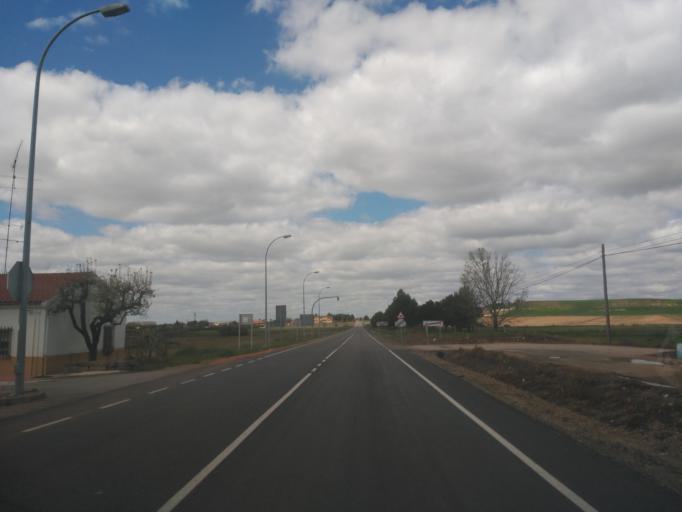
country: ES
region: Castille and Leon
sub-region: Provincia de Salamanca
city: Villamayor
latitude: 41.0013
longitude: -5.6983
